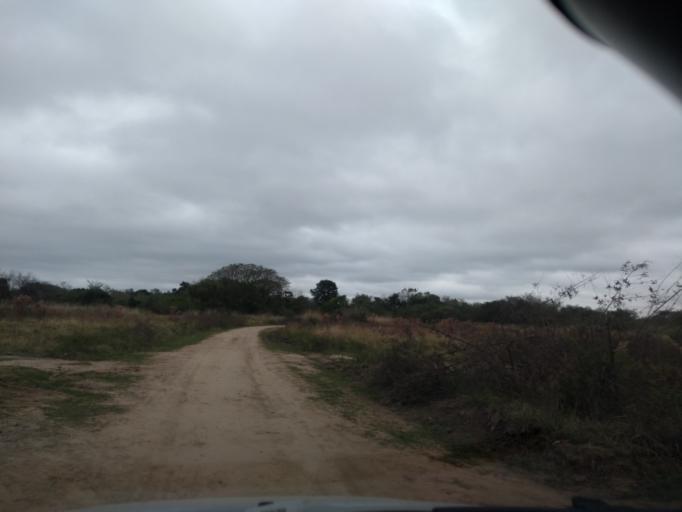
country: AR
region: Chaco
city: Barranqueras
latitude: -27.4362
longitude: -58.9386
